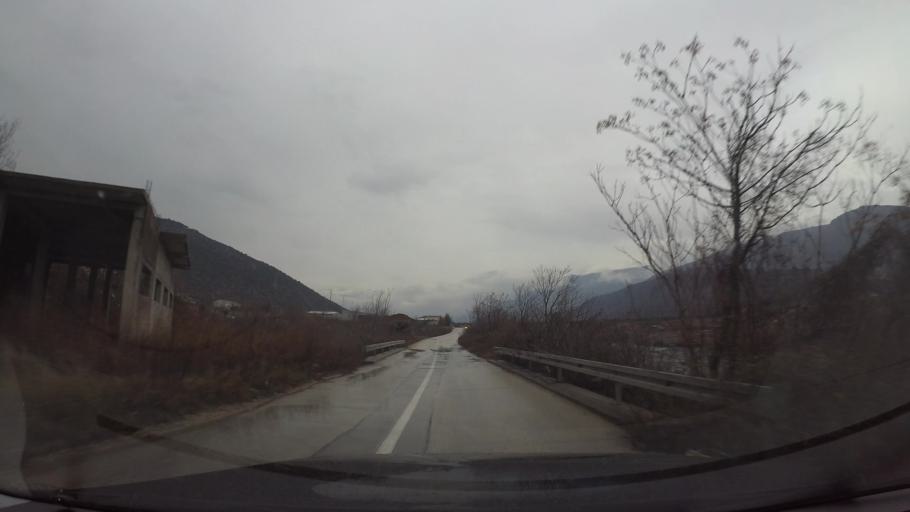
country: BA
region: Federation of Bosnia and Herzegovina
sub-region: Hercegovacko-Bosanski Kanton
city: Mostar
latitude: 43.3652
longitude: 17.8110
